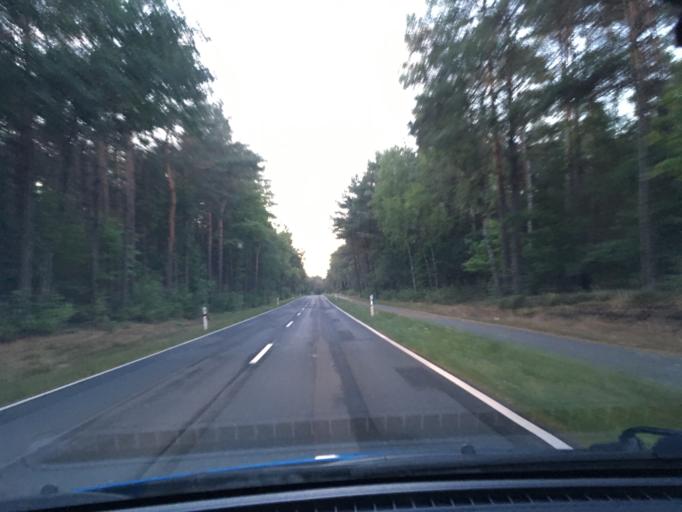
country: DE
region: Lower Saxony
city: Fassberg
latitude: 52.9078
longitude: 10.1527
